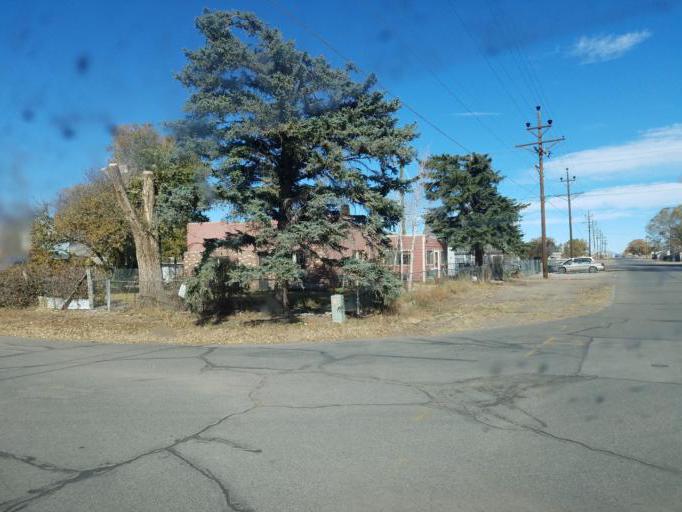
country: US
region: Colorado
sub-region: Alamosa County
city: Alamosa
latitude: 37.4702
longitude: -105.8574
